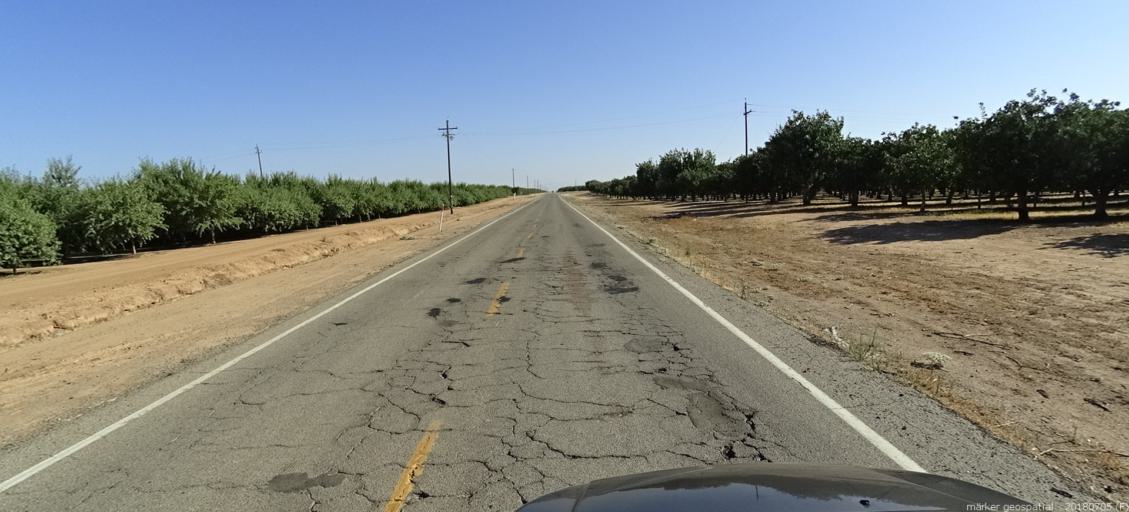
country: US
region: California
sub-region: Madera County
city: Madera Acres
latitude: 37.0664
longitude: -120.0746
